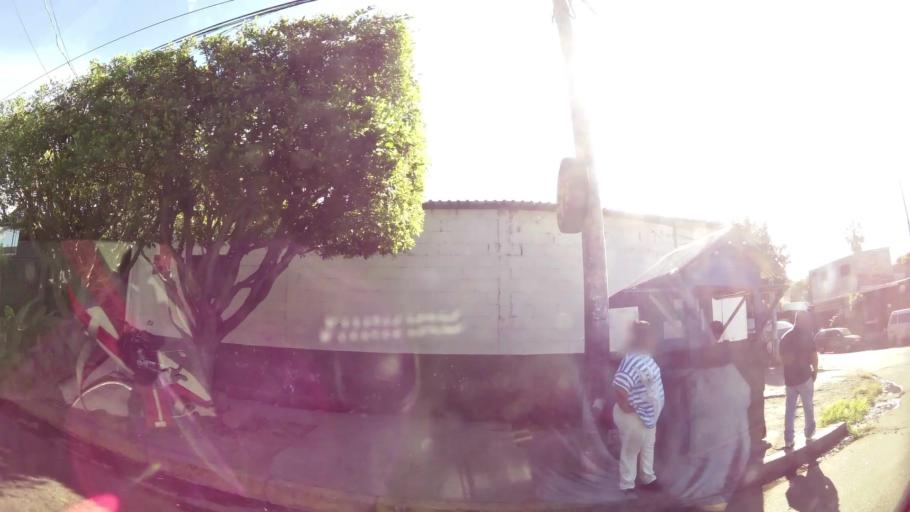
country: SV
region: La Libertad
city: Santa Tecla
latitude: 13.6875
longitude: -89.2943
